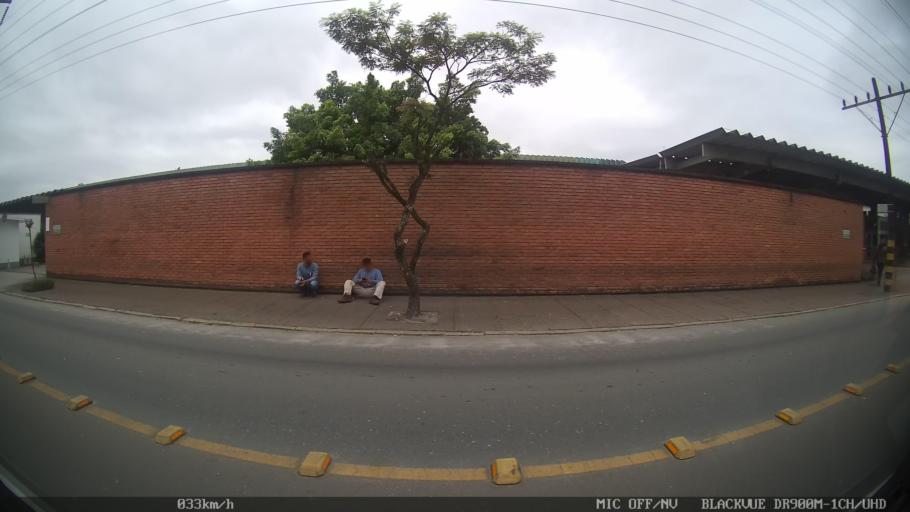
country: BR
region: Santa Catarina
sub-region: Joinville
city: Joinville
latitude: -26.2613
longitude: -48.8725
